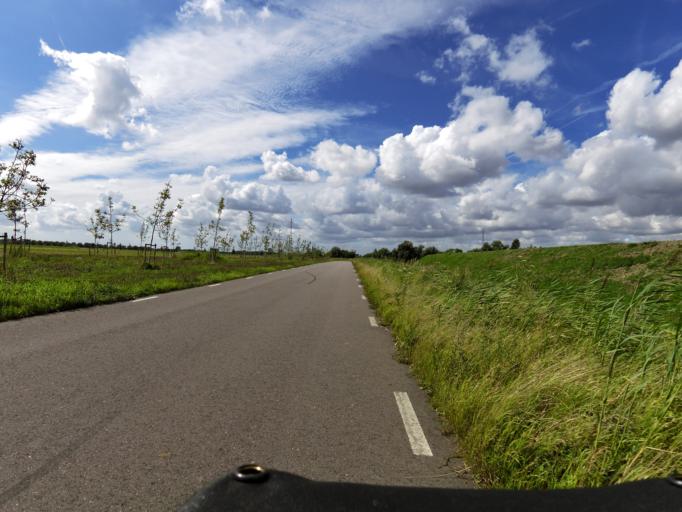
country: NL
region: South Holland
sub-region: Gemeente Oud-Beijerland
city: Oud-Beijerland
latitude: 51.8356
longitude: 4.3884
